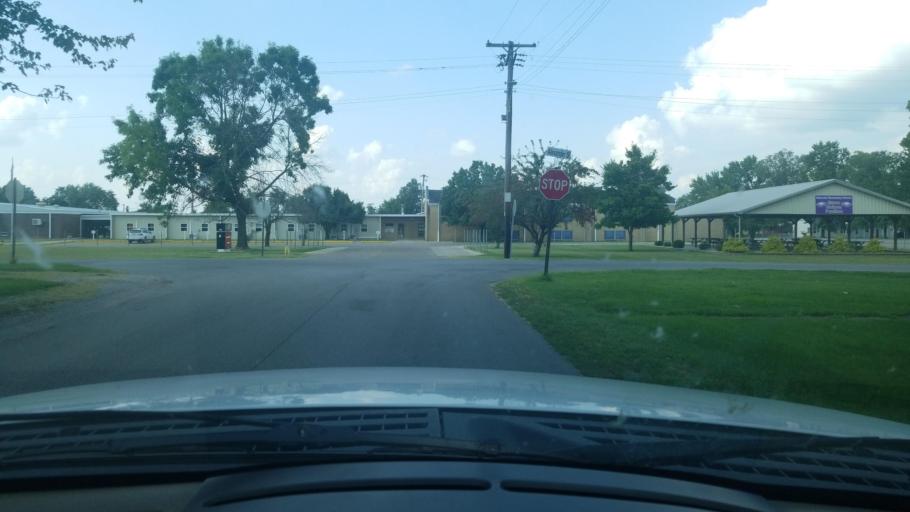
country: US
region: Illinois
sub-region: Saline County
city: Eldorado
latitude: 37.8268
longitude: -88.4363
